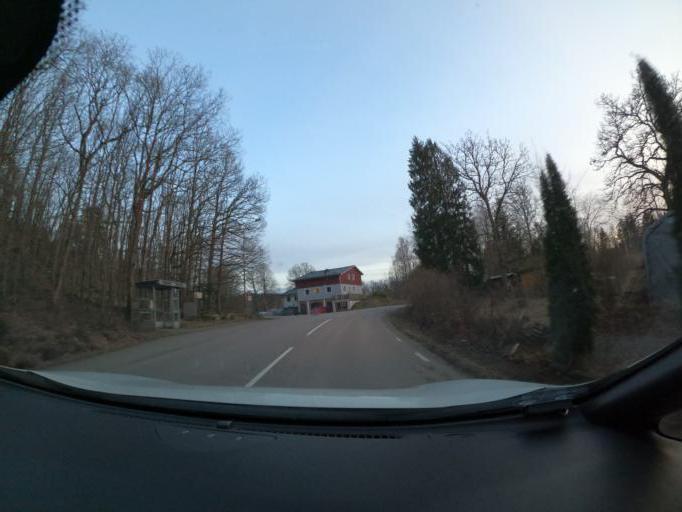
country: SE
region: Vaestra Goetaland
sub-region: Harryda Kommun
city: Landvetter
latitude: 57.6367
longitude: 12.1816
